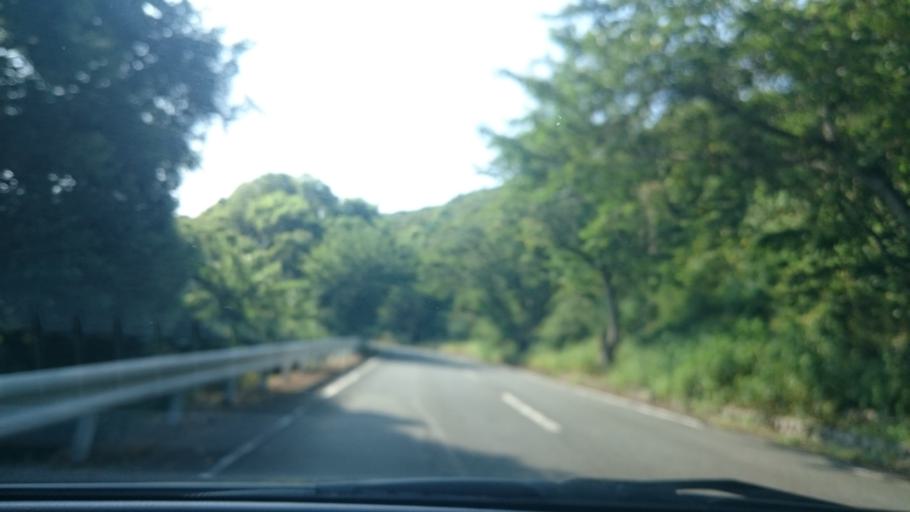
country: JP
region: Shizuoka
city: Heda
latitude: 34.9825
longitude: 138.7728
